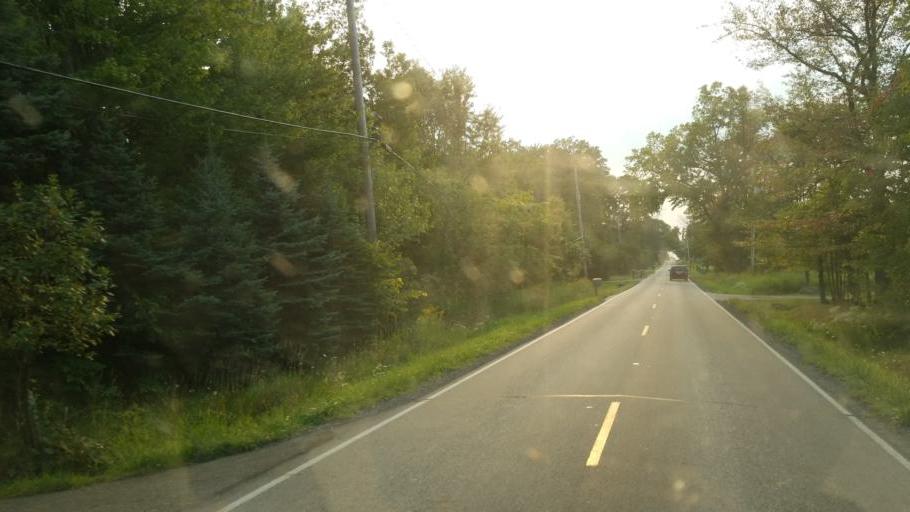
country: US
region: Ohio
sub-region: Portage County
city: Hiram
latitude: 41.3869
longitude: -81.1295
